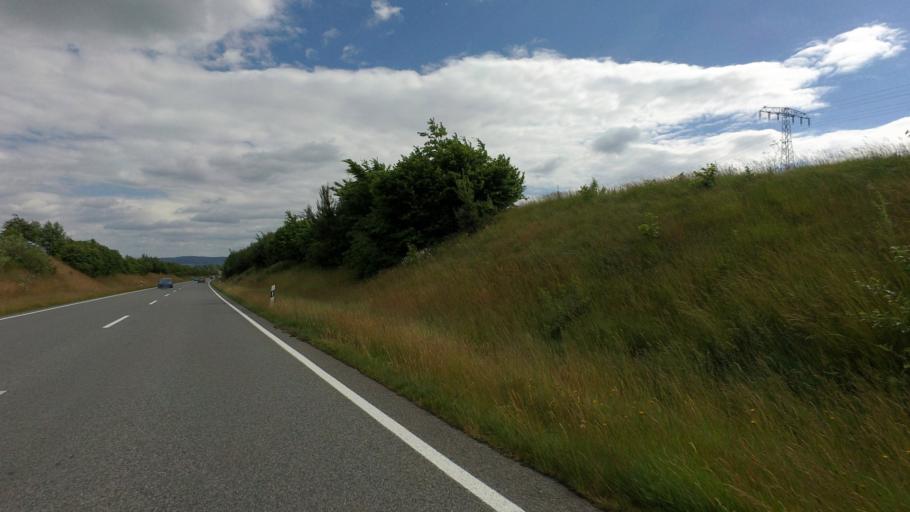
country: DE
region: Saxony
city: Berthelsdorf
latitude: 51.0769
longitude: 14.1929
